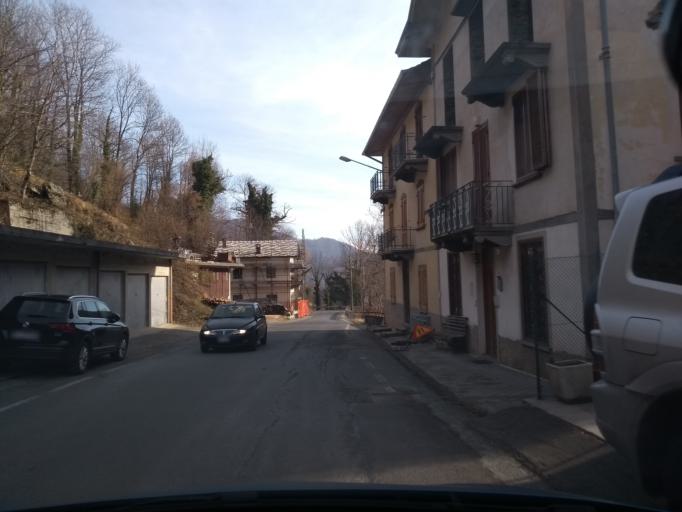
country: IT
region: Piedmont
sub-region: Provincia di Torino
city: Cantoira
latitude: 45.3212
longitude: 7.3553
